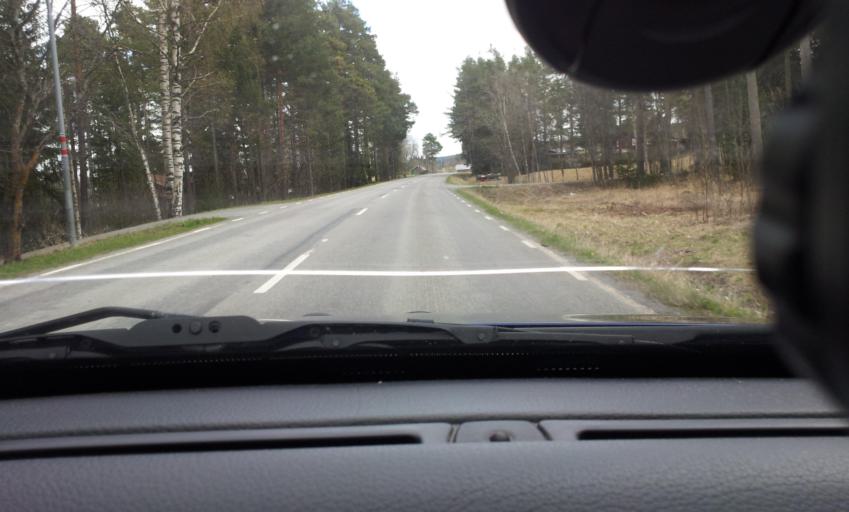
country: SE
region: Jaemtland
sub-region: OEstersunds Kommun
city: Ostersund
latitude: 63.1486
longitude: 14.6050
